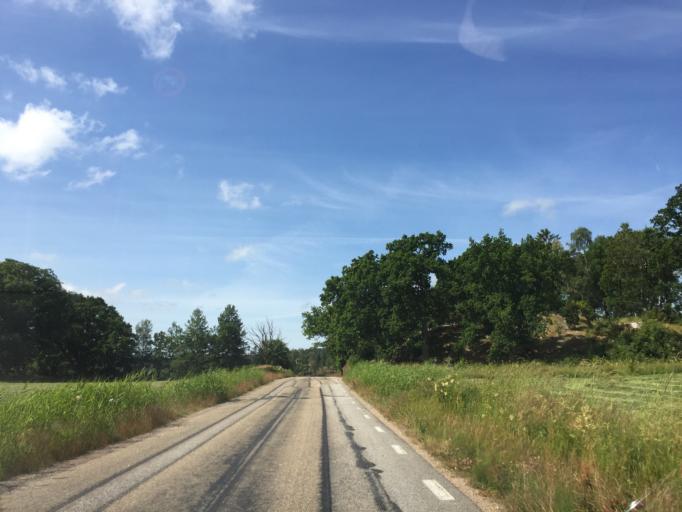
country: SE
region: Vaestra Goetaland
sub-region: Orust
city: Henan
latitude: 58.3132
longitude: 11.6818
